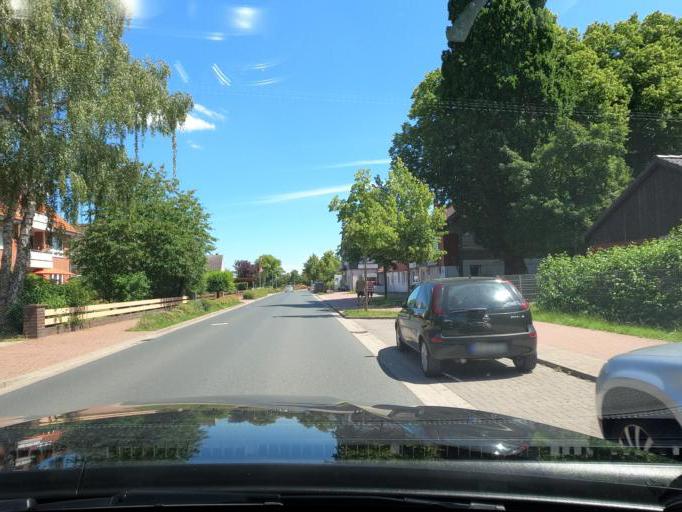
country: DE
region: Lower Saxony
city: Sehnde
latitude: 52.3511
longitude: 9.8944
